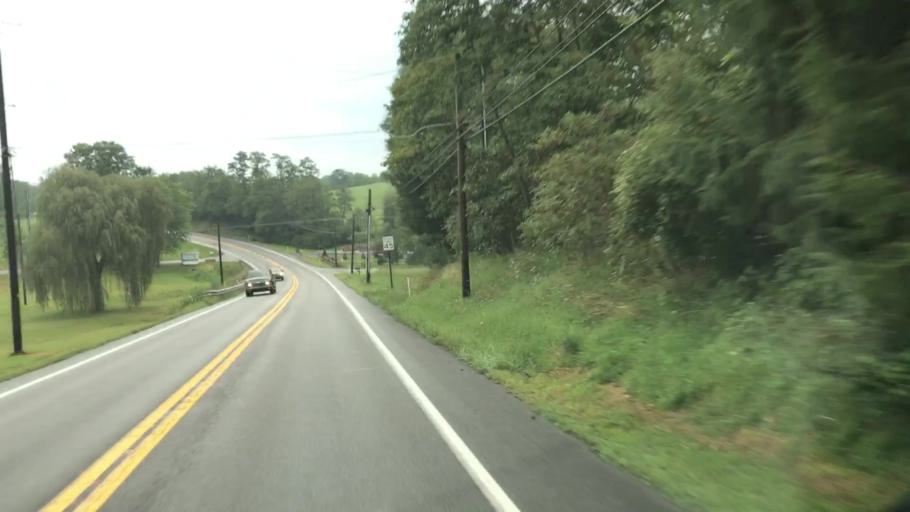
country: US
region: Pennsylvania
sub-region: Perry County
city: New Bloomfield
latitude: 40.3749
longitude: -77.1548
